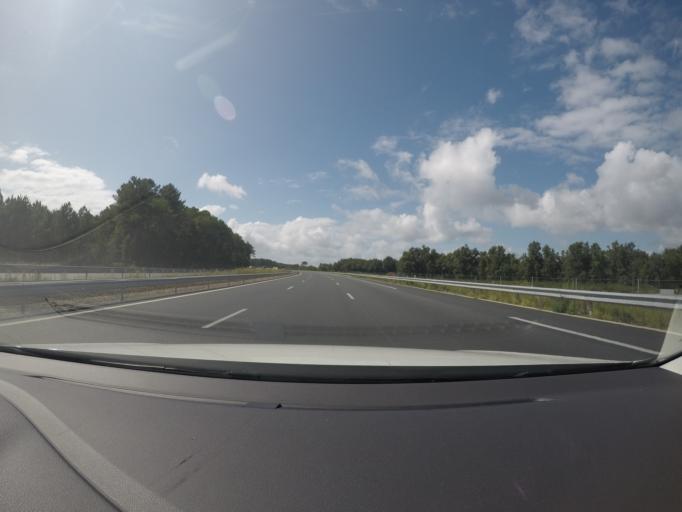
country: FR
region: Aquitaine
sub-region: Departement des Landes
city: Castets
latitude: 43.8677
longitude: -1.1561
